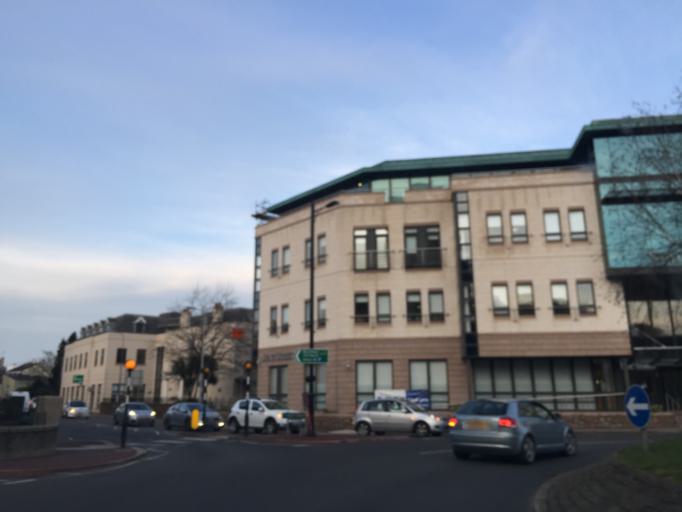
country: JE
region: St Helier
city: Saint Helier
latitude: 49.1805
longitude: -2.1035
